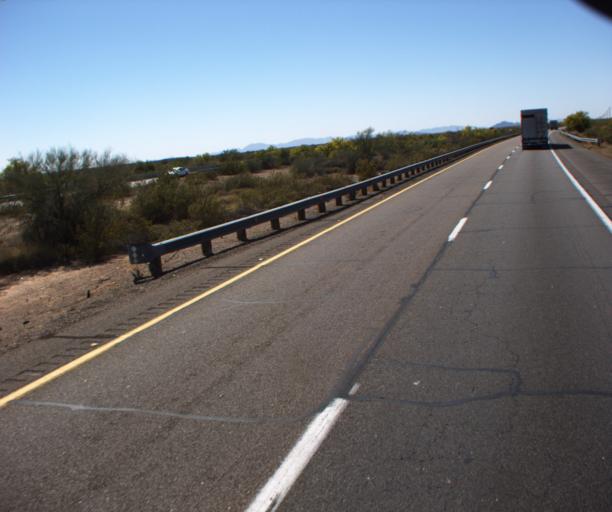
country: US
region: Arizona
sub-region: Maricopa County
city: Gila Bend
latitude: 32.8462
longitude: -113.2786
